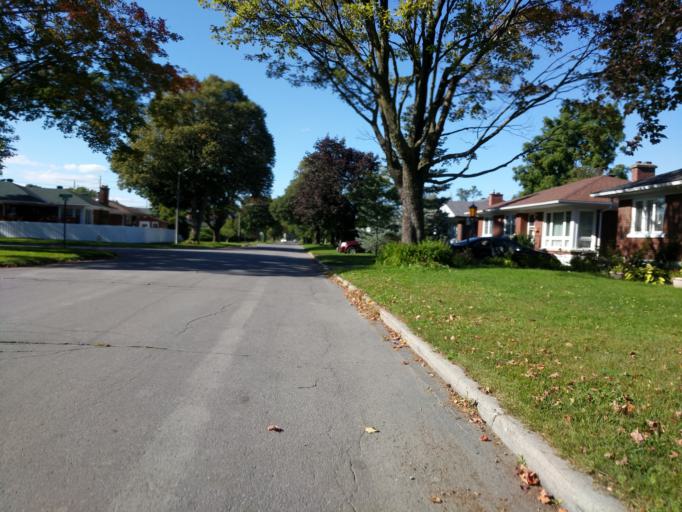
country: CA
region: Ontario
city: Bells Corners
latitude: 45.3583
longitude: -75.7615
